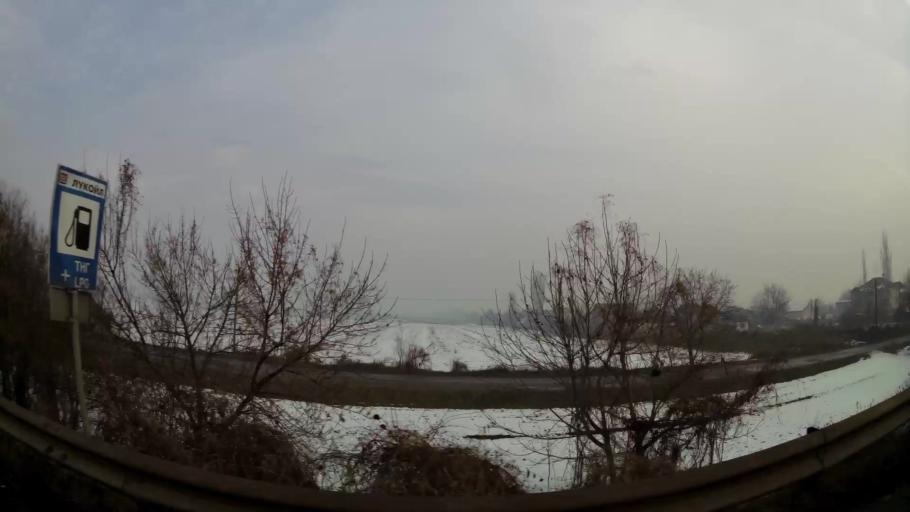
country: MK
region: Ilinden
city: Jurumleri
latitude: 41.9768
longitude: 21.5340
